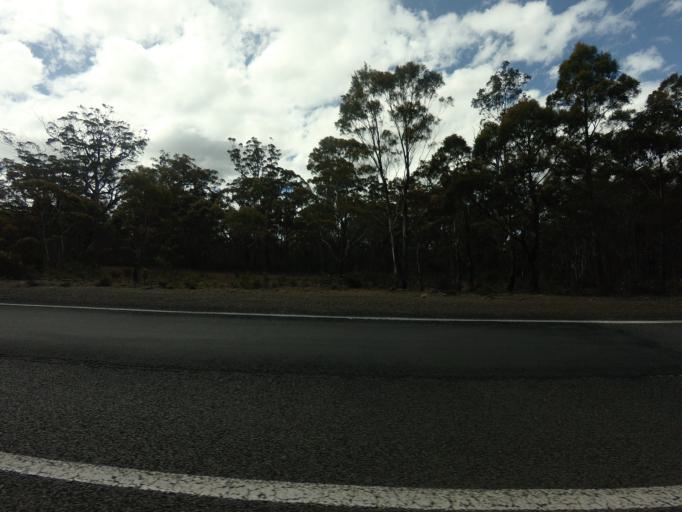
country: AU
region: Tasmania
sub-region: Break O'Day
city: St Helens
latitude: -42.0103
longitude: 147.8962
